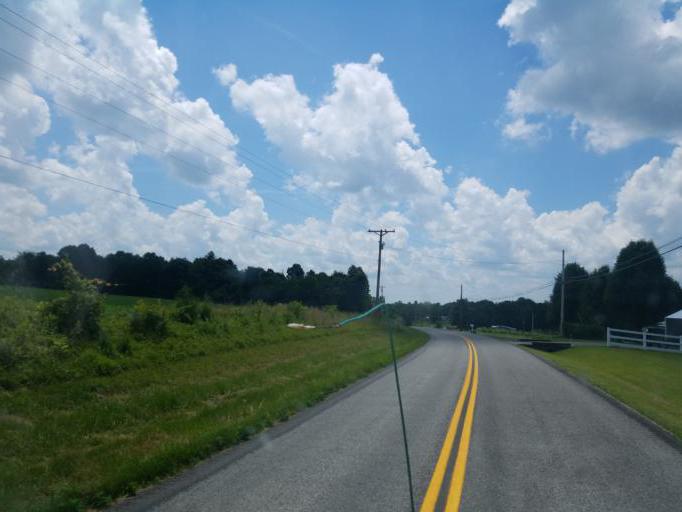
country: US
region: Kentucky
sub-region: Grayson County
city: Leitchfield
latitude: 37.4941
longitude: -86.4764
